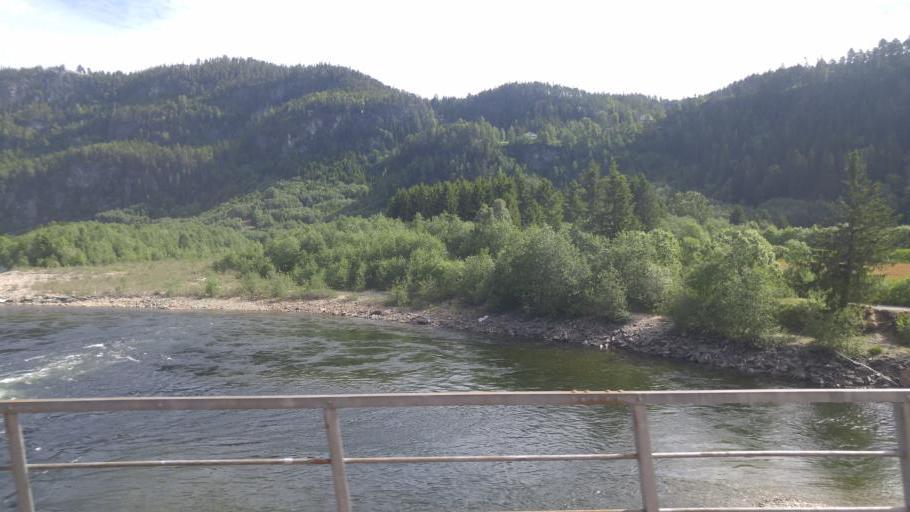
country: NO
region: Sor-Trondelag
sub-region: Midtre Gauldal
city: Storen
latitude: 63.0425
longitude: 10.2920
